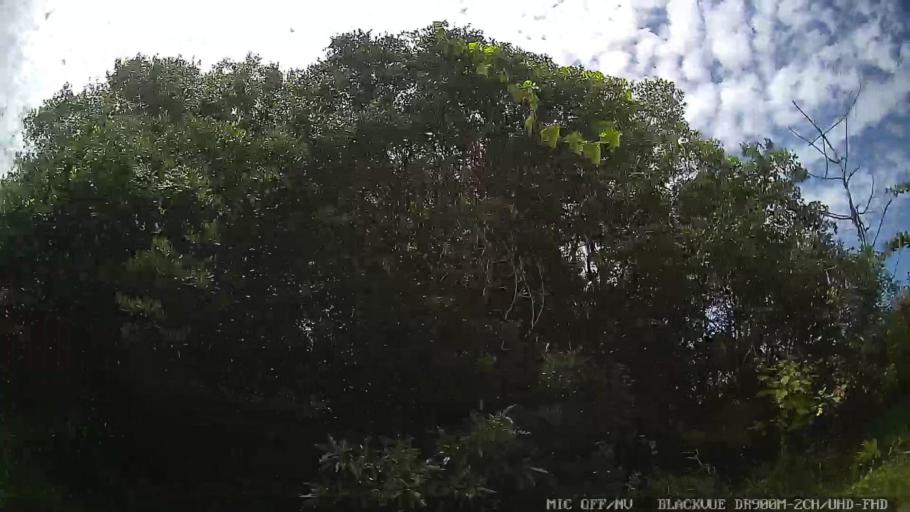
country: BR
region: Sao Paulo
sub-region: Iguape
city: Iguape
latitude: -24.7205
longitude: -47.5229
